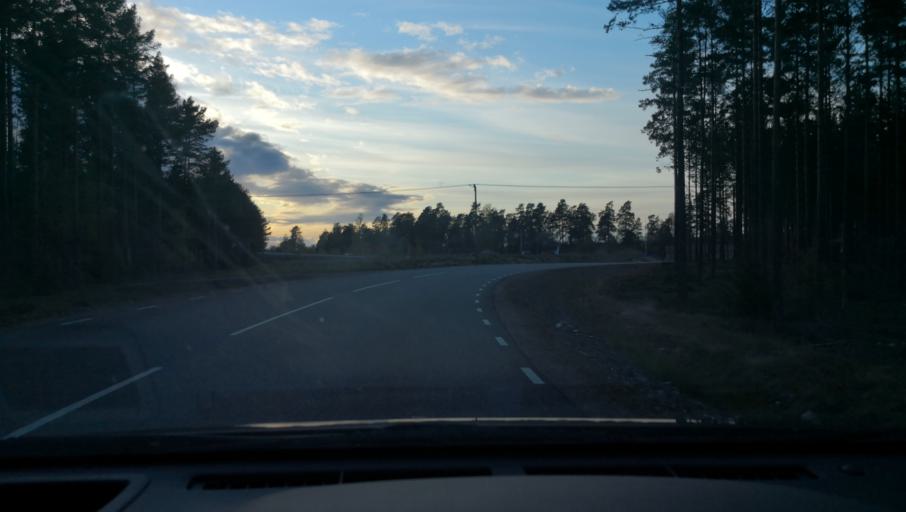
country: SE
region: OErebro
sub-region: Askersunds Kommun
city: Asbro
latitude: 58.9161
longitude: 15.0667
